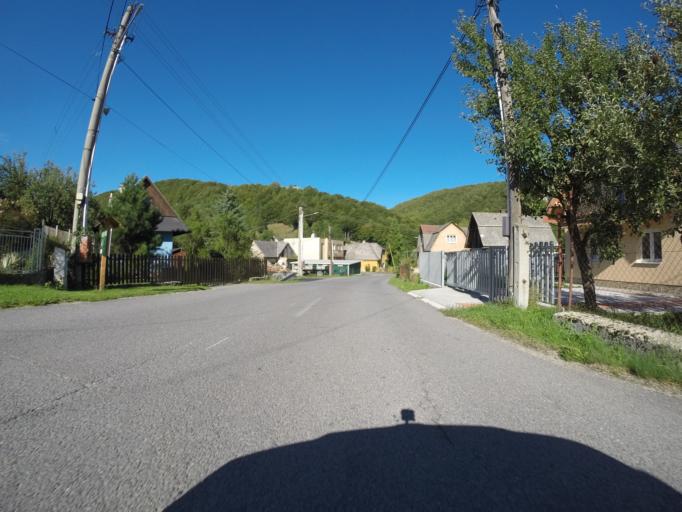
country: SK
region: Trenciansky
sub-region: Okres Povazska Bystrica
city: Povazska Bystrica
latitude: 48.9503
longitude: 18.4295
